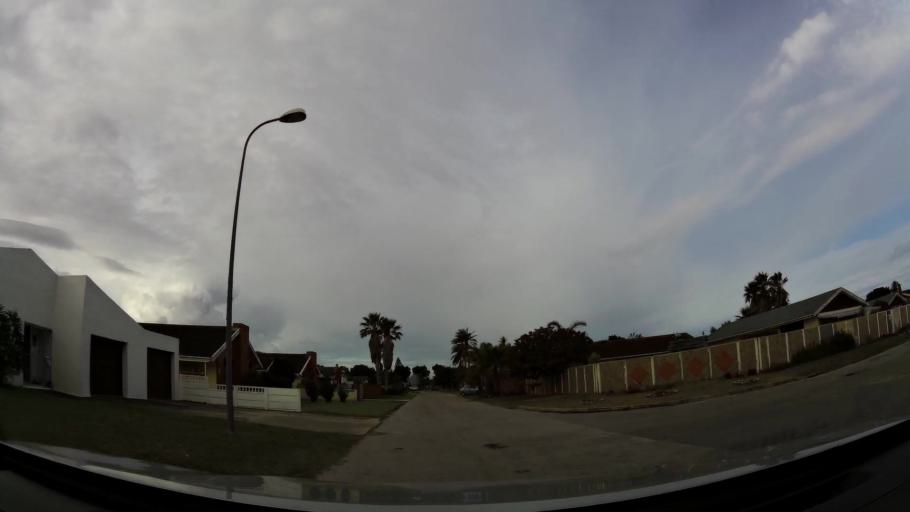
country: ZA
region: Eastern Cape
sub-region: Nelson Mandela Bay Metropolitan Municipality
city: Port Elizabeth
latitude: -33.9357
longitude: 25.4681
